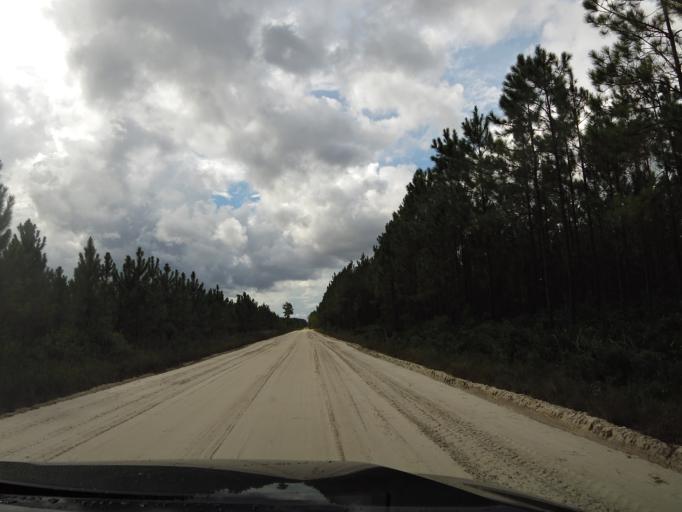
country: US
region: Florida
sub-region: Nassau County
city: Hilliard
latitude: 30.5947
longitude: -82.0551
